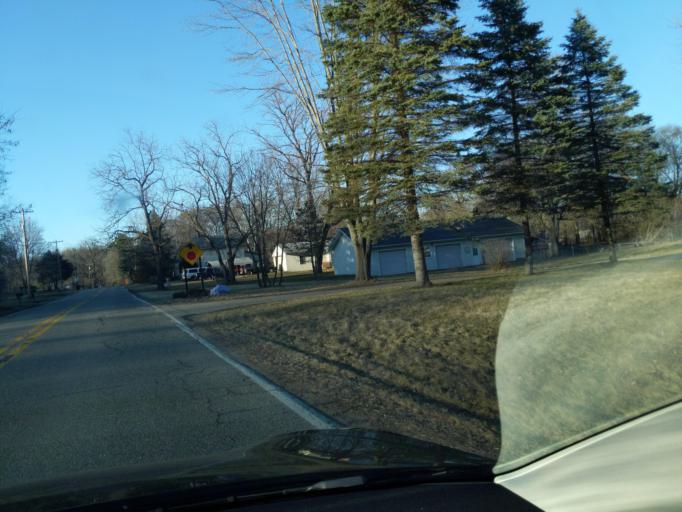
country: US
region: Michigan
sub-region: Livingston County
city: Pinckney
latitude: 42.4271
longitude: -84.0565
